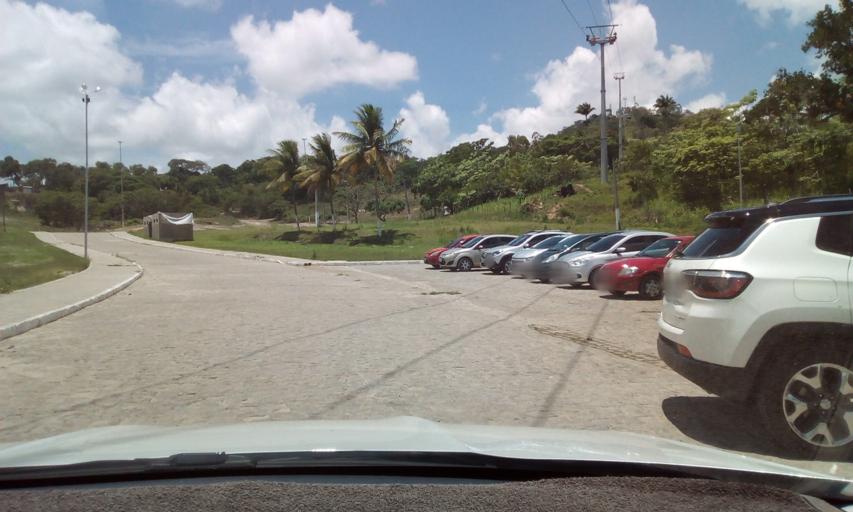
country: BR
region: Pernambuco
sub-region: Bonito
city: Bonito
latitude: -8.4708
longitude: -35.7276
